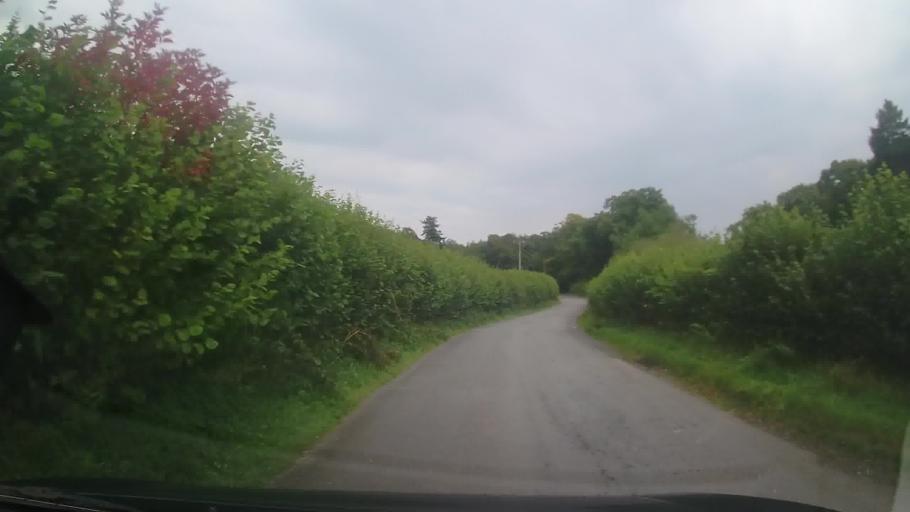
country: GB
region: Wales
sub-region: Sir Powys
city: Rhayader
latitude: 52.3043
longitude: -3.5296
